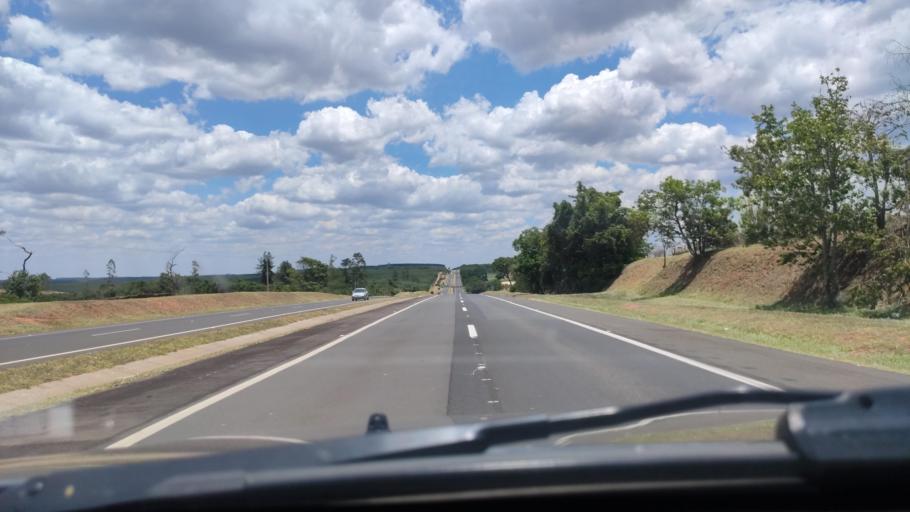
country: BR
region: Sao Paulo
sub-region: Duartina
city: Duartina
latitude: -22.5022
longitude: -49.2794
